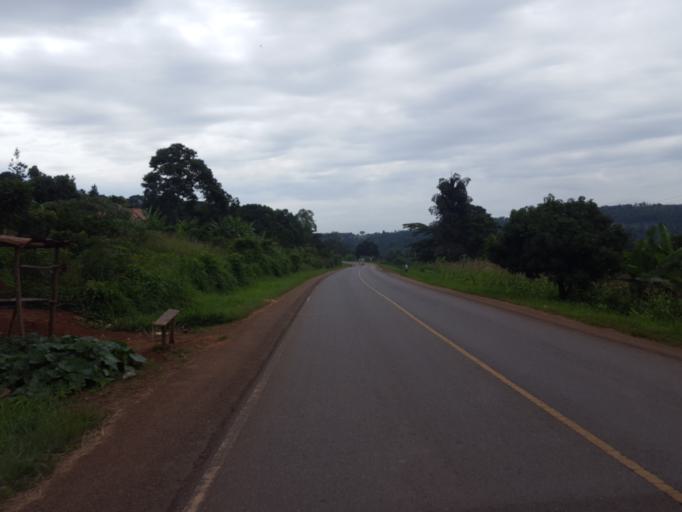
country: UG
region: Central Region
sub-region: Mityana District
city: Mityana
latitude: 0.6714
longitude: 32.0714
